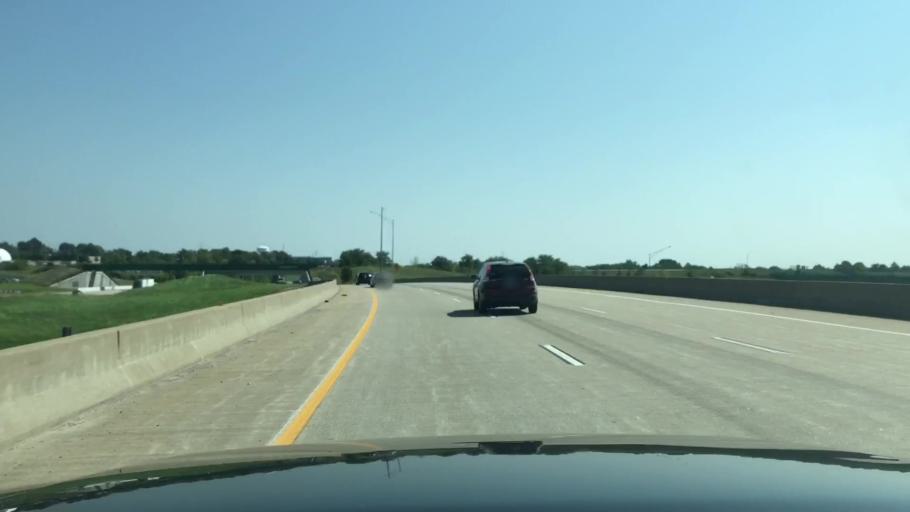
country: US
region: Missouri
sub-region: Saint Charles County
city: Saint Charles
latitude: 38.7539
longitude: -90.5480
